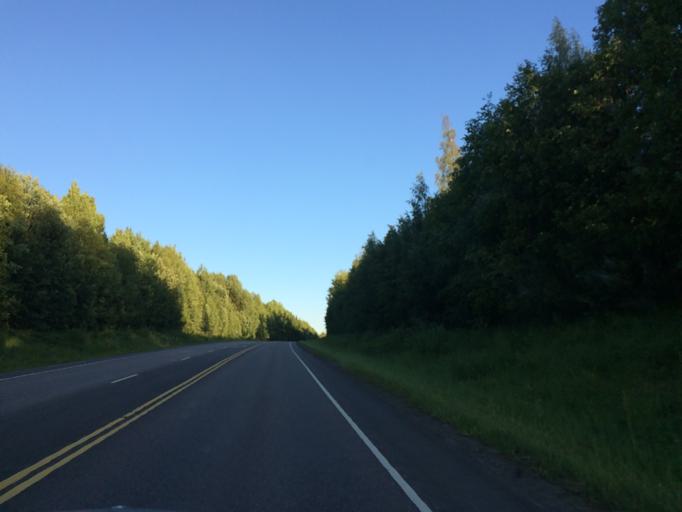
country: FI
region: Haeme
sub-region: Riihimaeki
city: Riihimaeki
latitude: 60.7639
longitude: 24.7128
